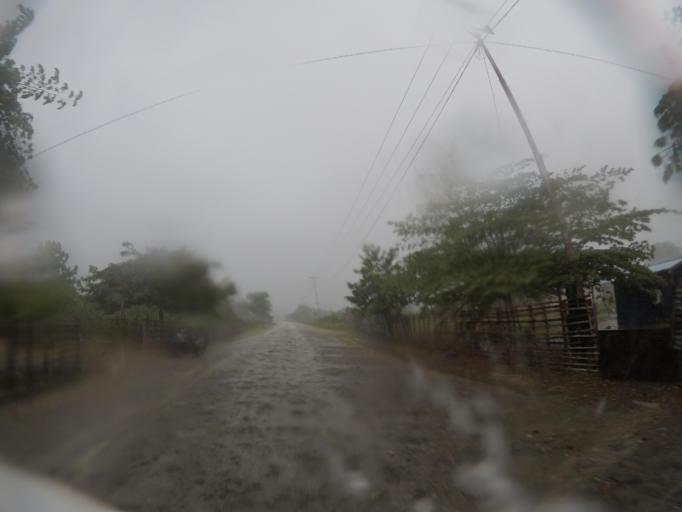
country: TL
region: Bobonaro
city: Maliana
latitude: -8.8570
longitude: 125.1006
